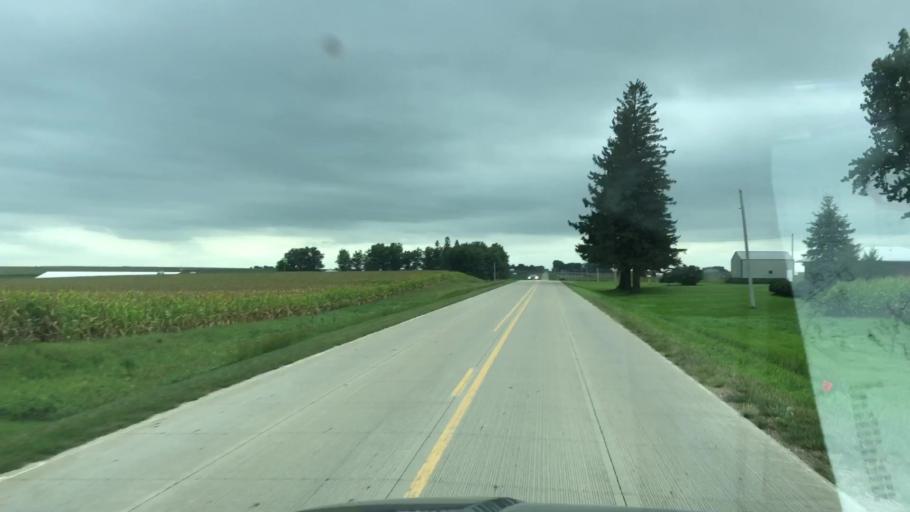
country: US
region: Iowa
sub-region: Sioux County
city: Alton
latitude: 43.1093
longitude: -95.9786
